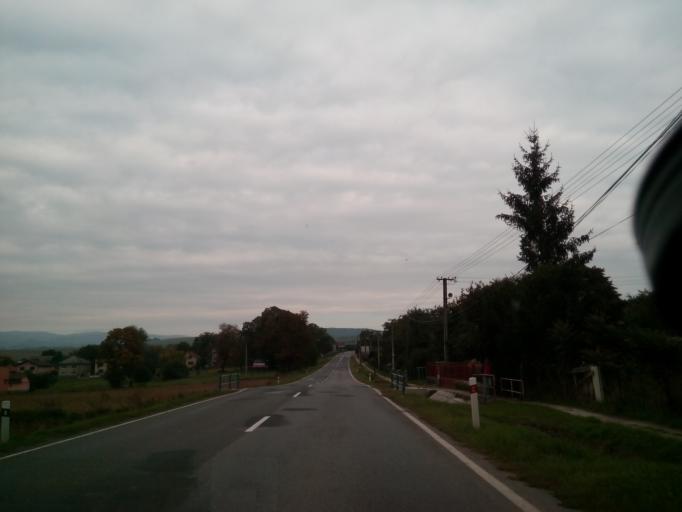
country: SK
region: Presovsky
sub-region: Okres Presov
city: Presov
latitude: 49.0852
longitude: 21.3151
